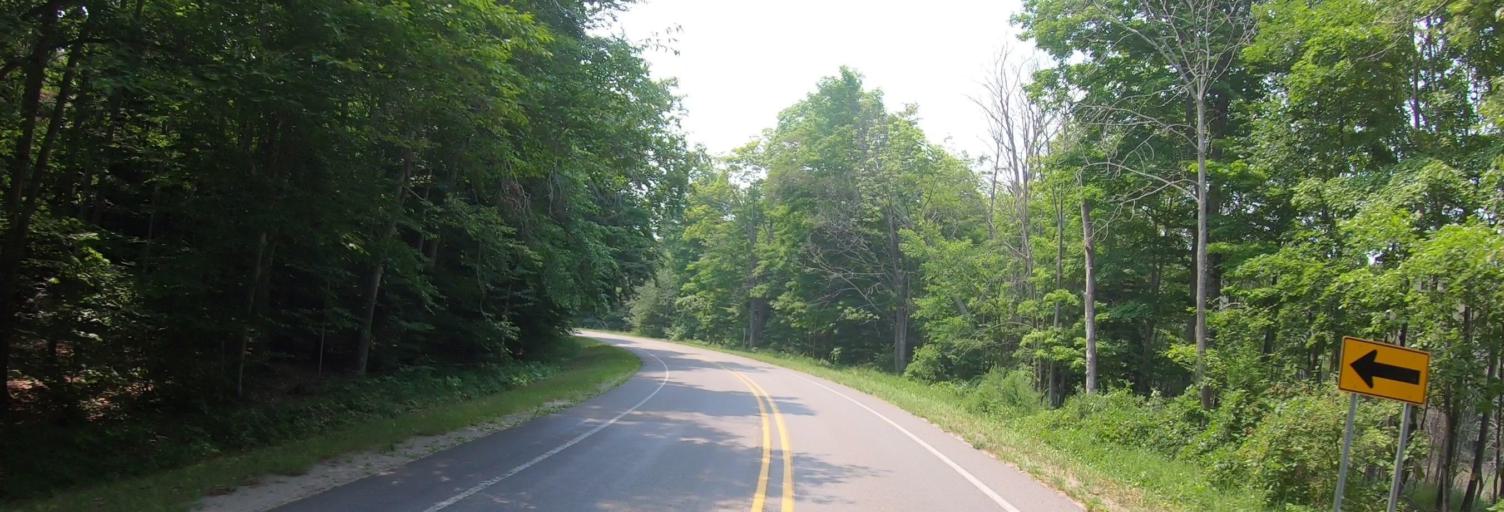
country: US
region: Michigan
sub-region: Leelanau County
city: Leland
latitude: 45.1593
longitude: -85.5865
